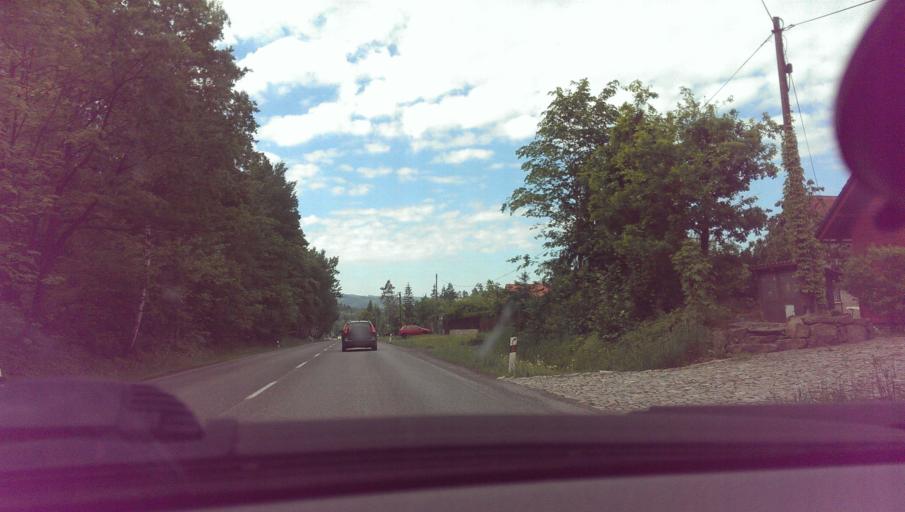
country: CZ
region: Zlin
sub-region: Okres Vsetin
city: Roznov pod Radhostem
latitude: 49.4762
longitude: 18.1644
